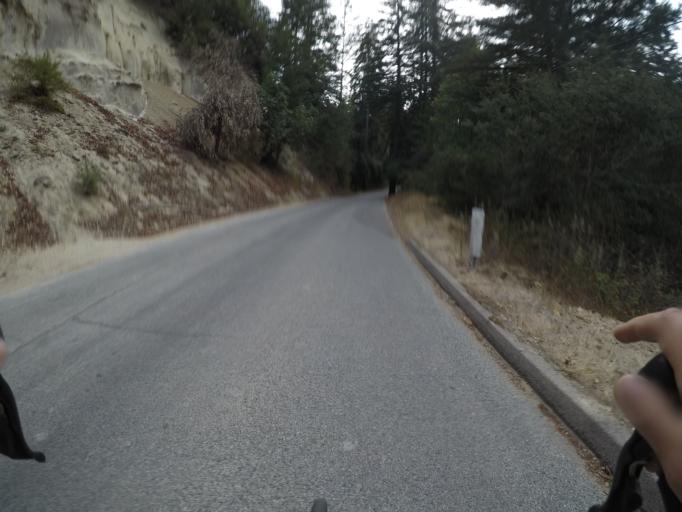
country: US
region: California
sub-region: Santa Cruz County
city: Scotts Valley
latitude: 37.0662
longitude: -122.0166
